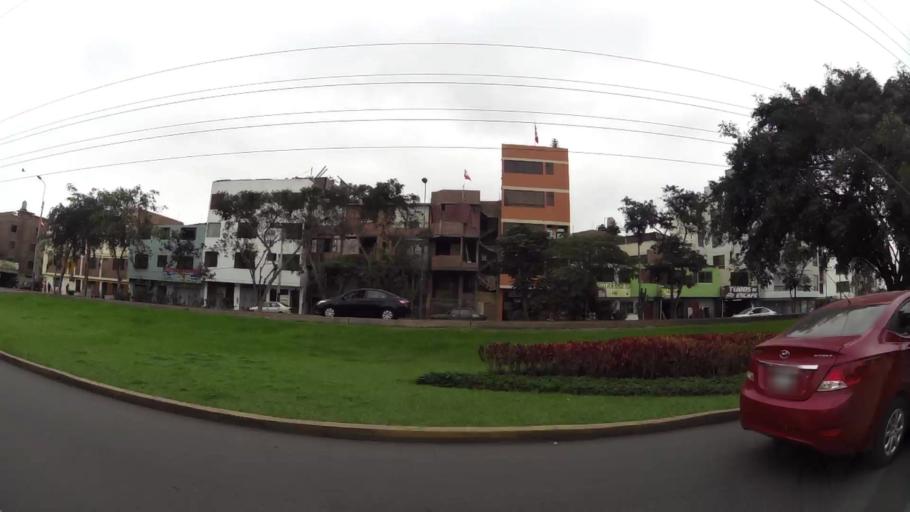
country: PE
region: Lima
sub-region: Lima
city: Surco
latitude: -12.1149
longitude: -76.9951
